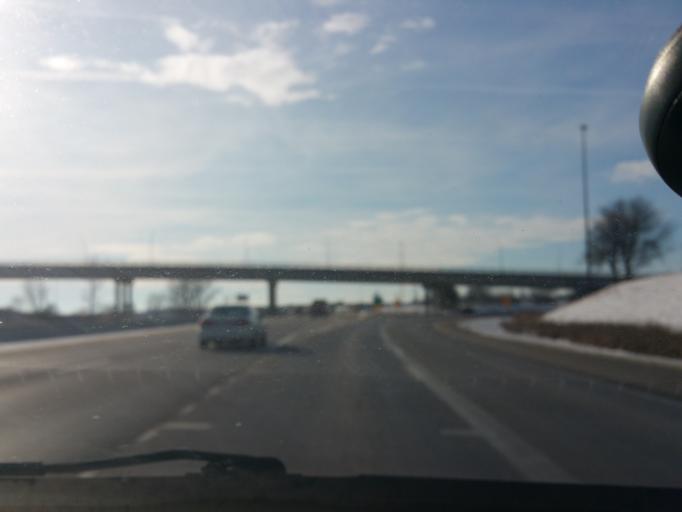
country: US
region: Iowa
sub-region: Polk County
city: Clive
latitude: 41.5974
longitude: -93.7772
